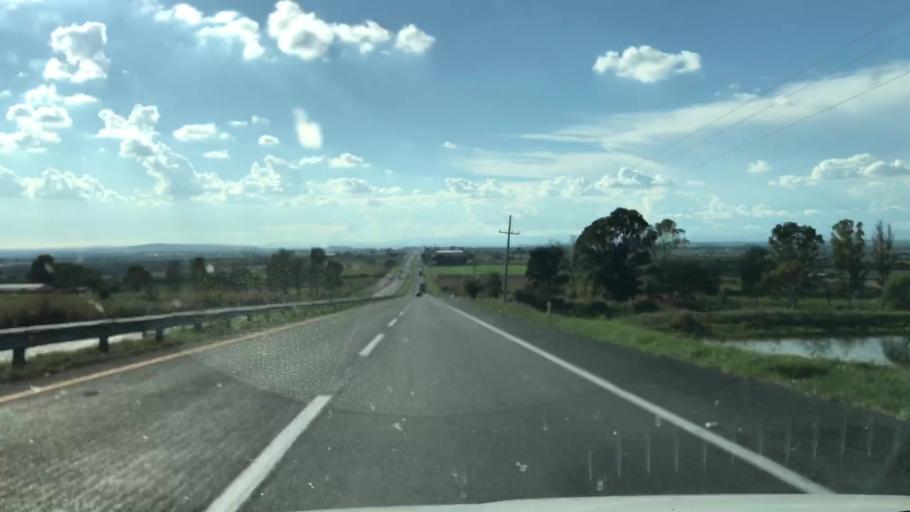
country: MX
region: Jalisco
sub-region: San Juan de los Lagos
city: Mezquitic de la Magdalena
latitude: 21.2897
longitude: -102.2199
